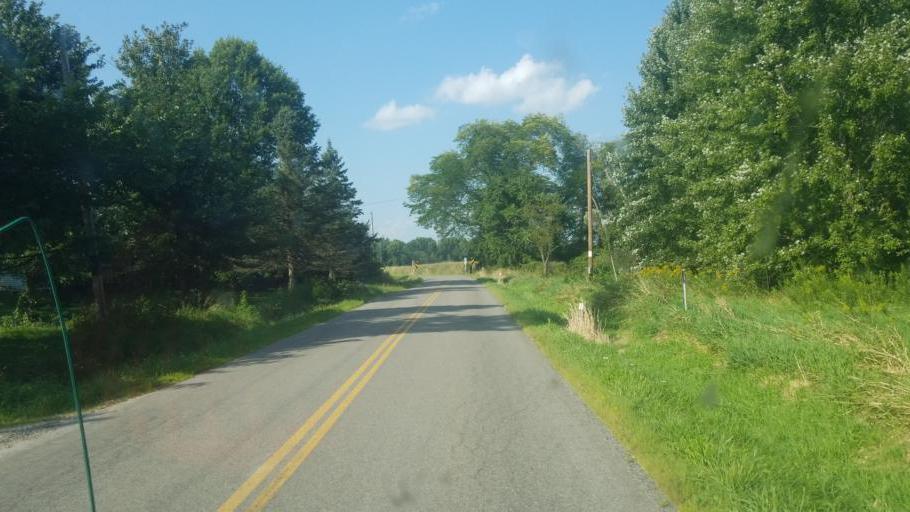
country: US
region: Ohio
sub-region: Medina County
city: Lodi
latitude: 41.0085
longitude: -82.0348
